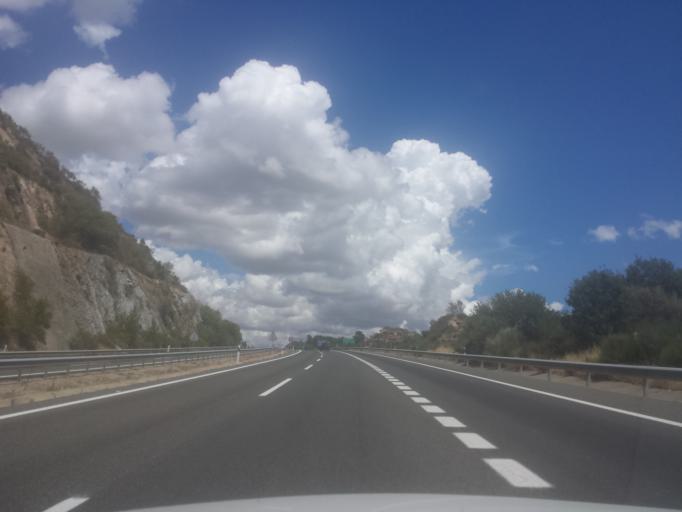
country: ES
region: Castille and Leon
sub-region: Provincia de Salamanca
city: Penacaballera
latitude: 40.3359
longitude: -5.8519
